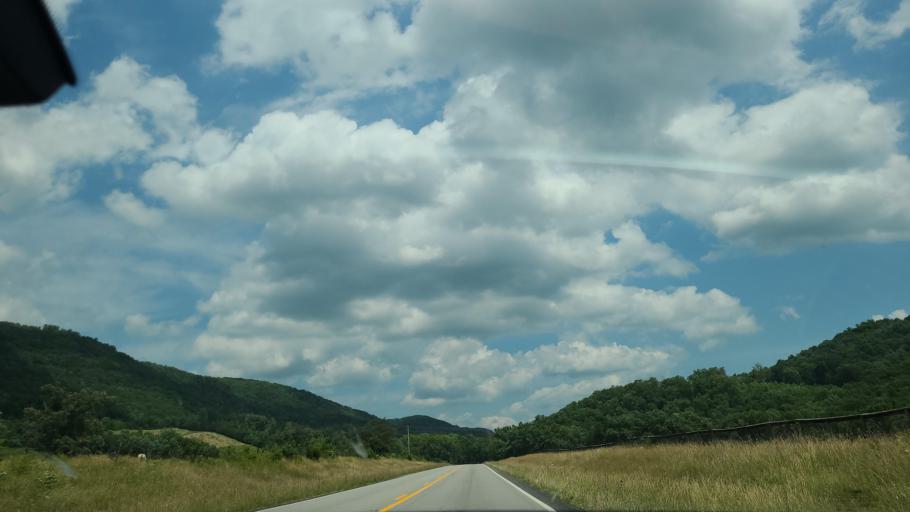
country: US
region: Tennessee
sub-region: Cumberland County
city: Lake Tansi
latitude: 35.7397
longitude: -85.0729
